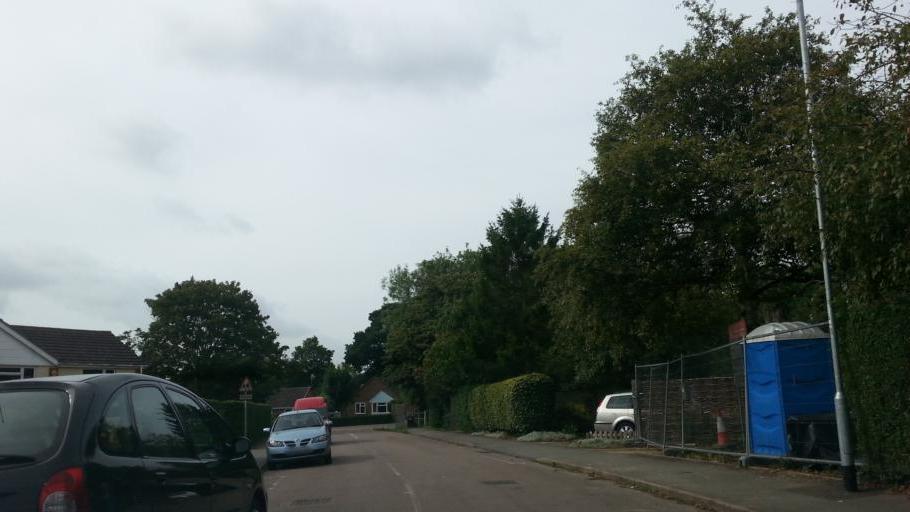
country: GB
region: England
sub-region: Cambridgeshire
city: Comberton
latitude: 52.1889
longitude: 0.0259
